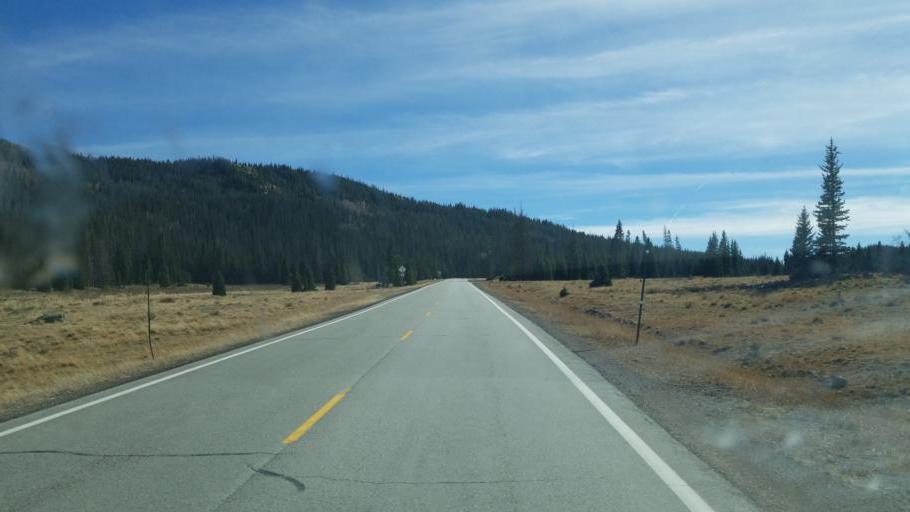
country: US
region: New Mexico
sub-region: Rio Arriba County
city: Chama
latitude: 37.0932
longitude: -106.3788
